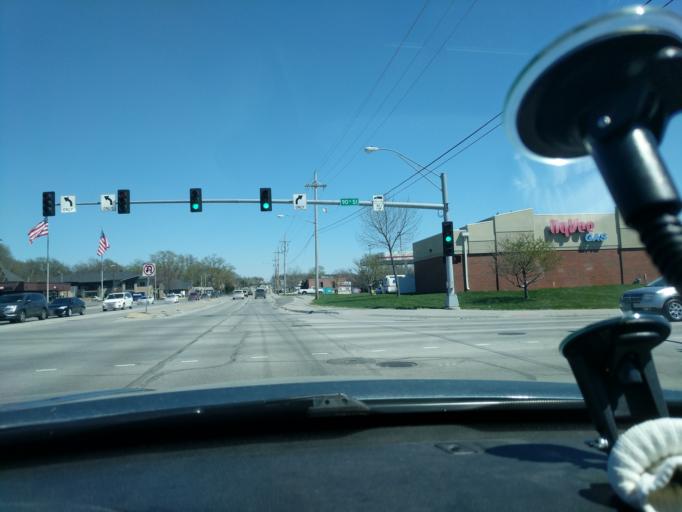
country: US
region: Nebraska
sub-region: Douglas County
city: Ralston
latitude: 41.2342
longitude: -96.0529
